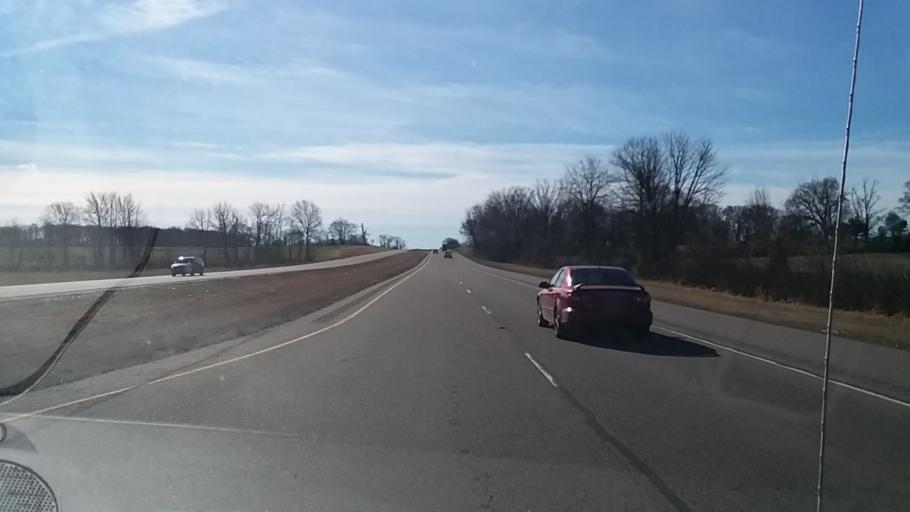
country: US
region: Tennessee
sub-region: Crockett County
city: Alamo
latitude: 35.8759
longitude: -89.2208
